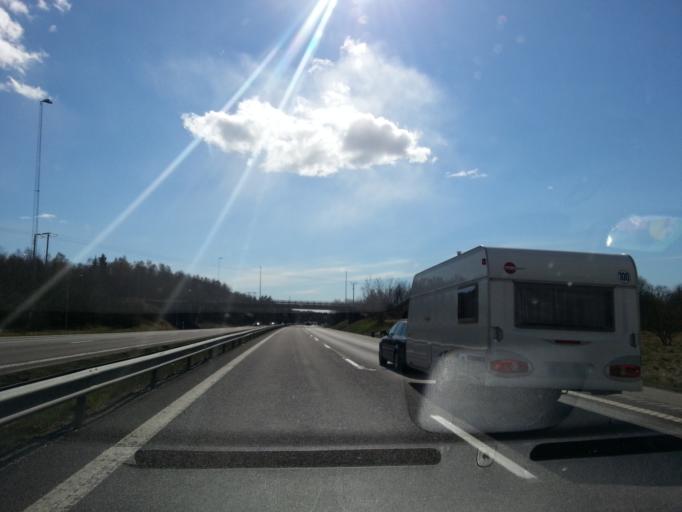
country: SE
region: Vaestra Goetaland
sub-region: Stenungsunds Kommun
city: Stora Hoga
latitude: 58.0582
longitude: 11.8801
